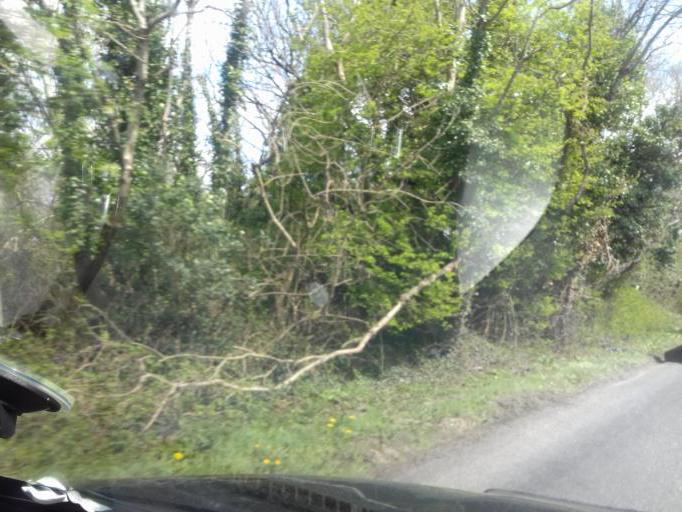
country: GB
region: Northern Ireland
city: Lisnaskea
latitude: 54.2070
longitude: -7.4874
